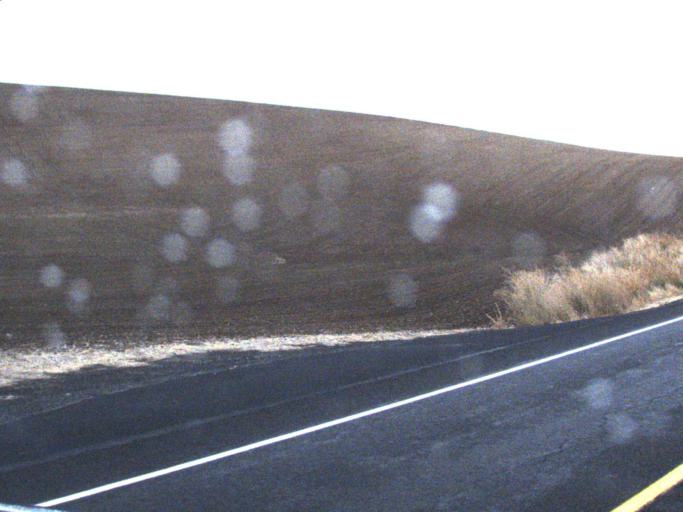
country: US
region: Washington
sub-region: Whitman County
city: Colfax
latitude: 46.8113
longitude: -117.5876
